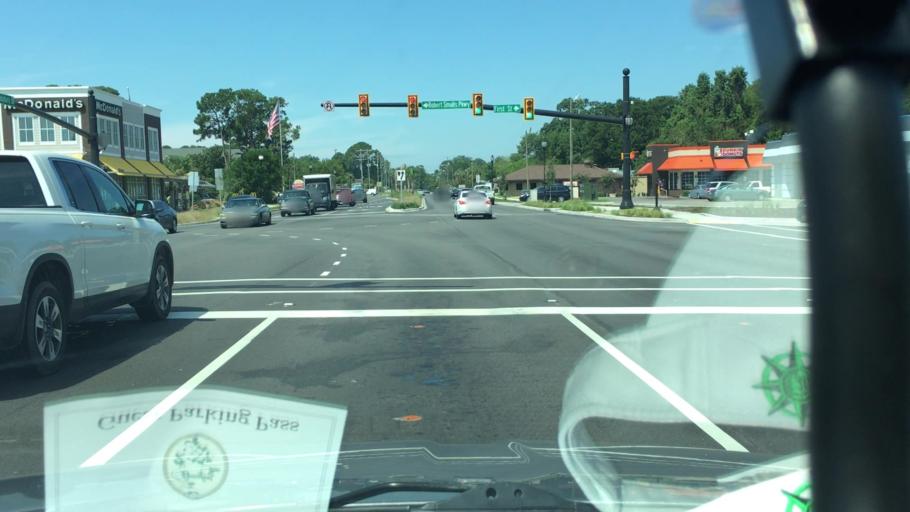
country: US
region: South Carolina
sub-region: Beaufort County
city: Burton
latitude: 32.4406
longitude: -80.7049
